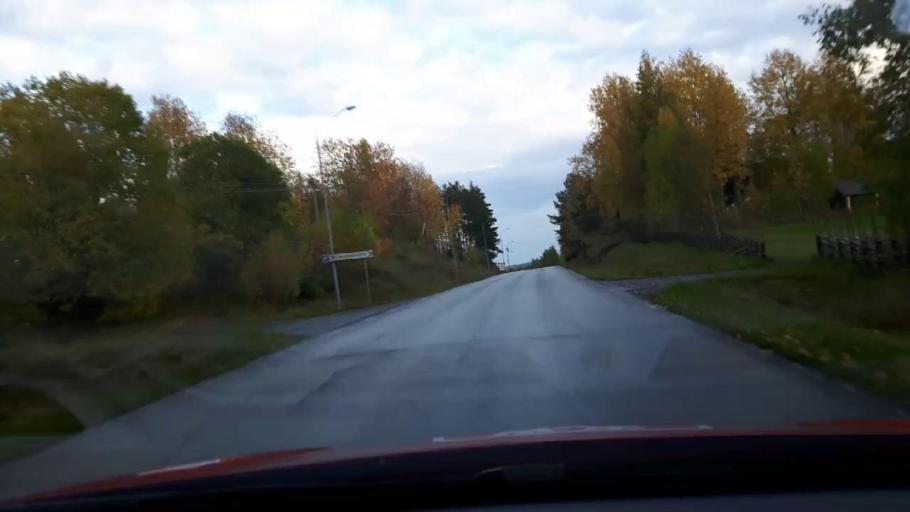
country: SE
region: Jaemtland
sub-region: OEstersunds Kommun
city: Lit
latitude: 63.3188
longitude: 14.8226
